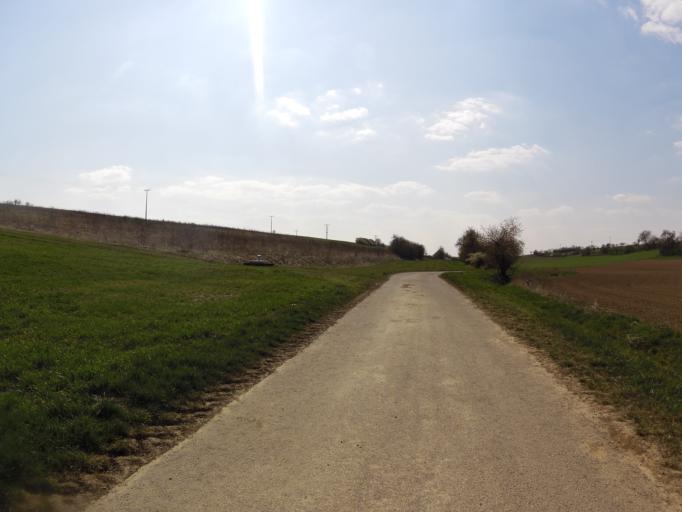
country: DE
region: Bavaria
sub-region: Regierungsbezirk Unterfranken
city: Mainstockheim
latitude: 49.8196
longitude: 10.1187
